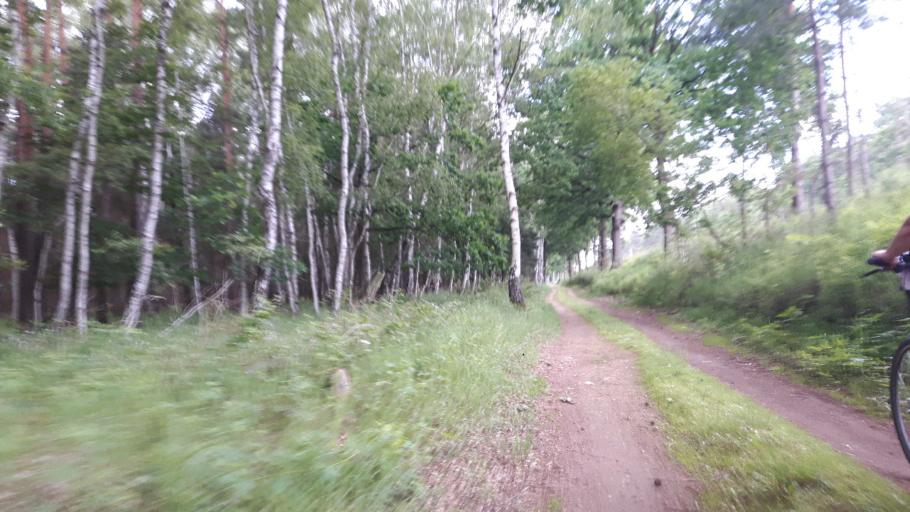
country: DE
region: Saxony-Anhalt
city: Radis
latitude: 51.7704
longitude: 12.5269
